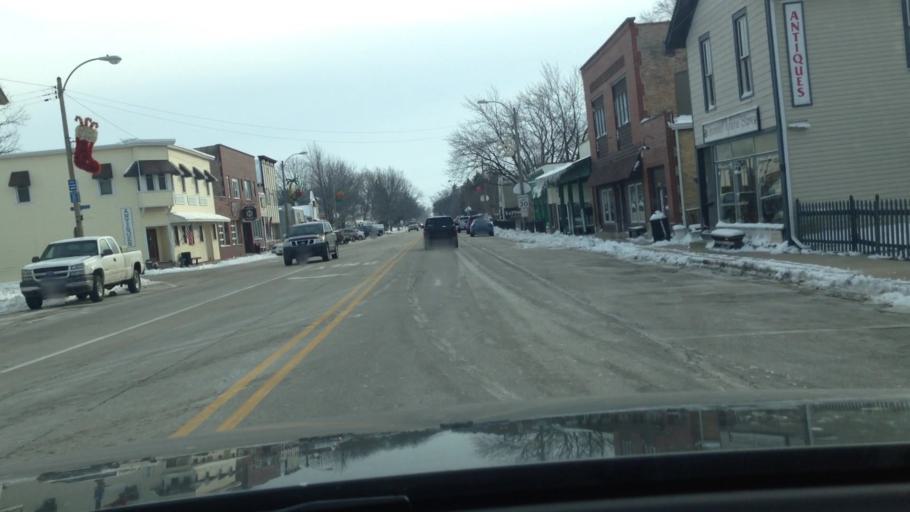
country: US
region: Illinois
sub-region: McHenry County
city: Hebron
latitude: 42.4718
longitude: -88.4328
